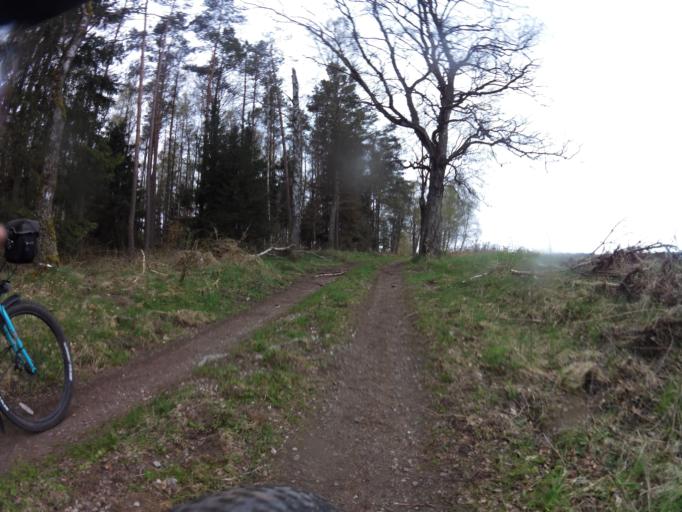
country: PL
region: West Pomeranian Voivodeship
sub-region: Powiat koszalinski
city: Polanow
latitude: 54.0799
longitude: 16.6104
